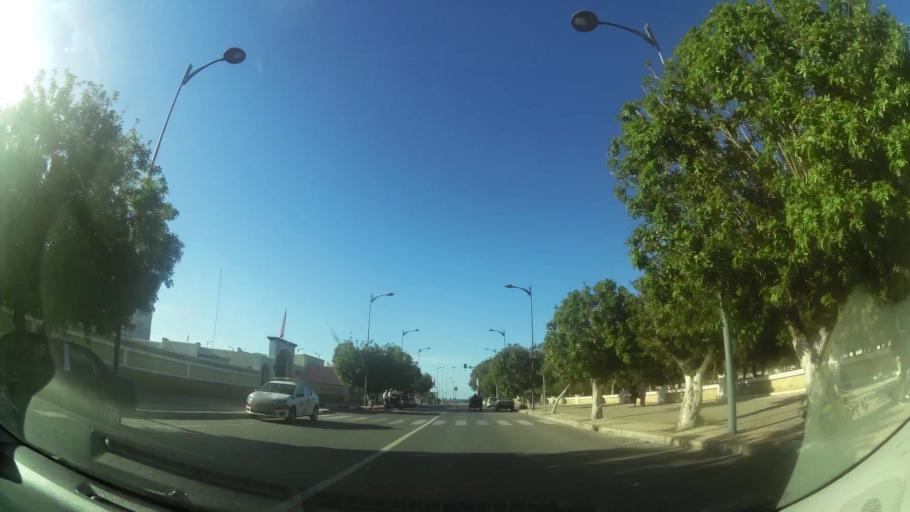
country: MA
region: Oriental
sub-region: Berkane-Taourirt
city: Madagh
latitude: 35.0827
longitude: -2.2154
